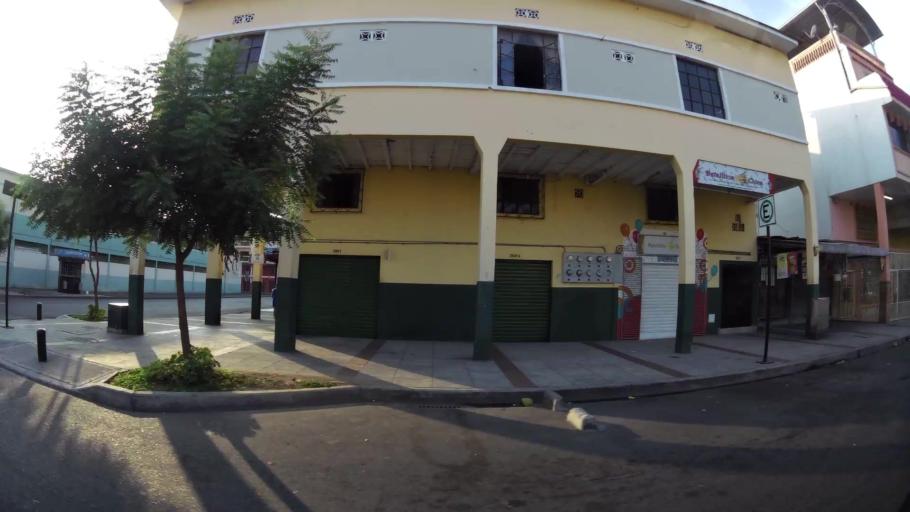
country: EC
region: Guayas
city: Guayaquil
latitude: -2.2099
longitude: -79.9008
